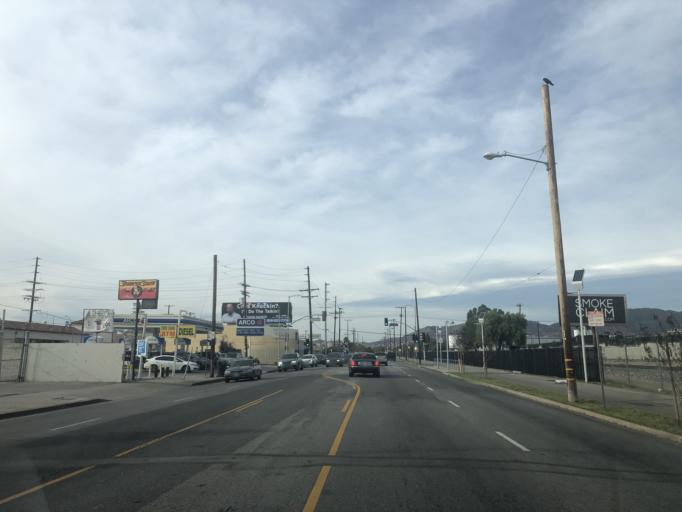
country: US
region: California
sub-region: Los Angeles County
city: San Fernando
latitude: 34.2739
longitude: -118.4303
